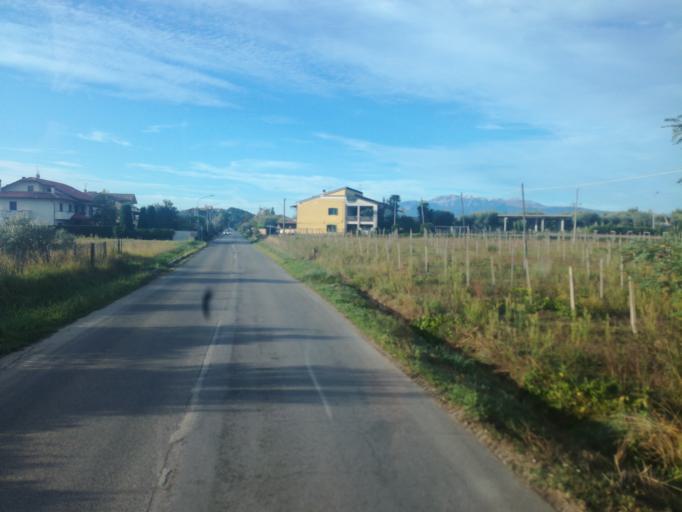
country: IT
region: Abruzzo
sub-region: Provincia di Chieti
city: Miglianico
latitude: 42.3813
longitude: 14.2897
